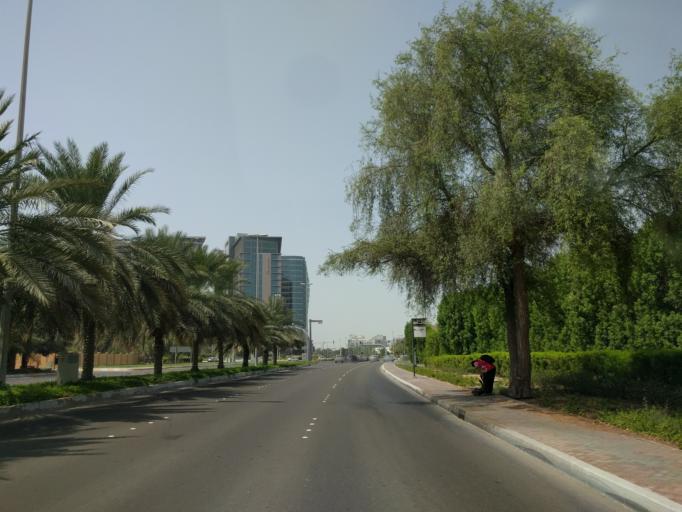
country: AE
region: Abu Dhabi
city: Abu Dhabi
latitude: 24.4268
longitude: 54.4286
